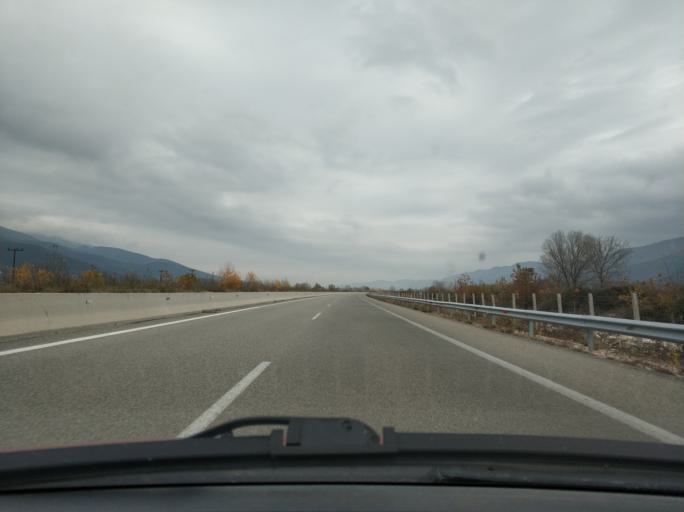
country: GR
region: East Macedonia and Thrace
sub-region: Nomos Kavalas
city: Nikisiani
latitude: 40.8471
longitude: 24.1292
